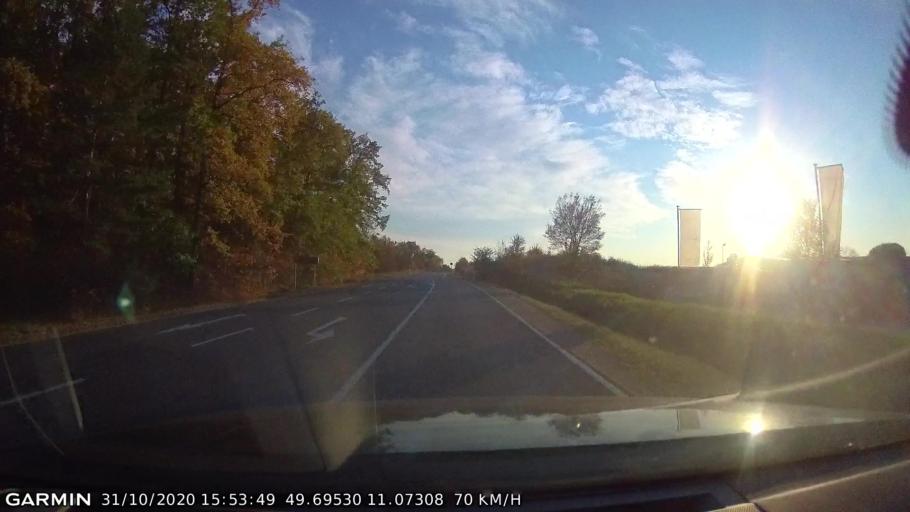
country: DE
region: Bavaria
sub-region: Upper Franconia
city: Forchheim
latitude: 49.6951
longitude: 11.0725
